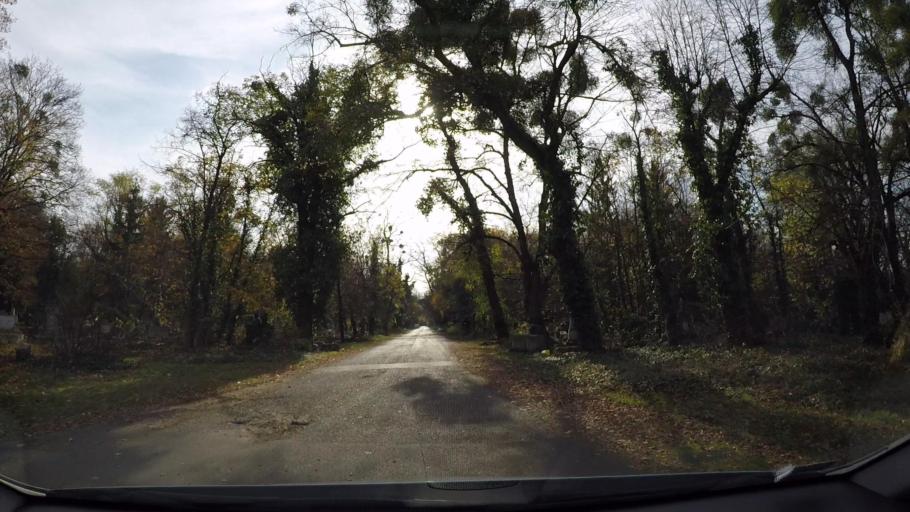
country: HU
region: Budapest
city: Budapest XVIII. keruelet
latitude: 47.4683
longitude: 19.1886
